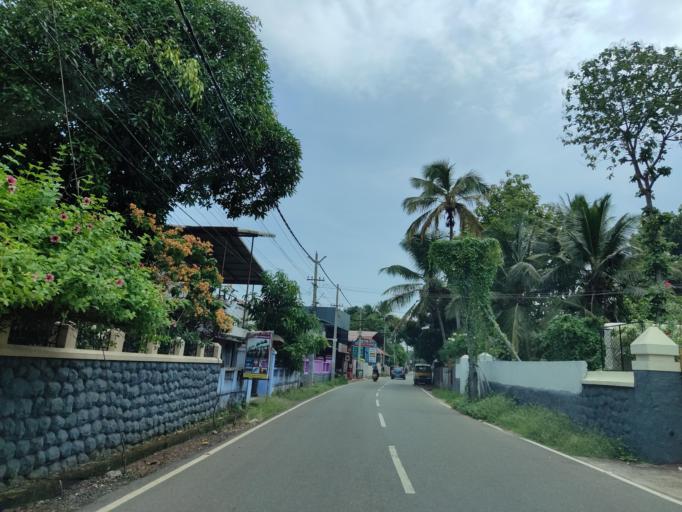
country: IN
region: Kerala
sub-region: Alappuzha
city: Chengannur
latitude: 9.3174
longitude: 76.6126
